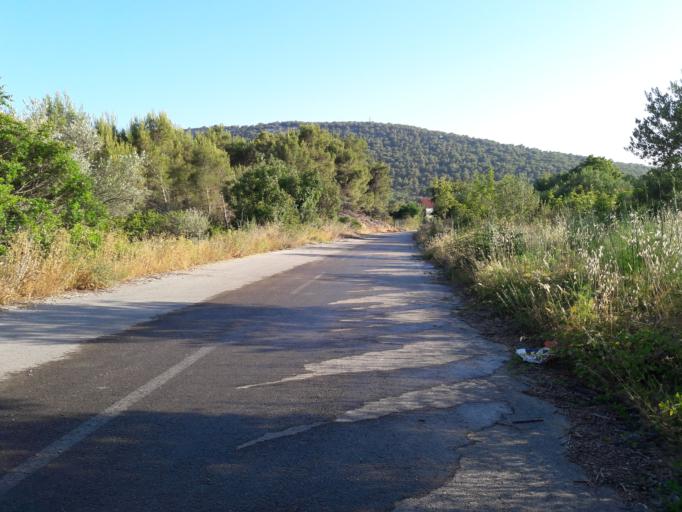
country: HR
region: Sibensko-Kniniska
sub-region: Grad Sibenik
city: Sibenik
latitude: 43.6960
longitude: 15.8462
